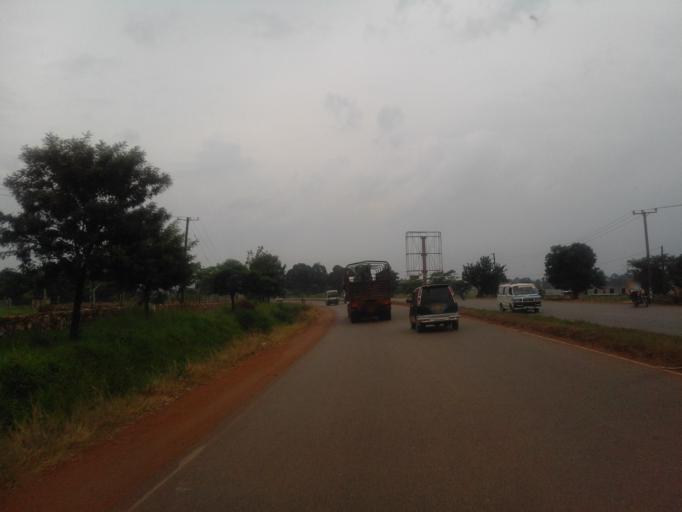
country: UG
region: Eastern Region
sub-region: Jinja District
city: Jinja
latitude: 0.4422
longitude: 33.2153
